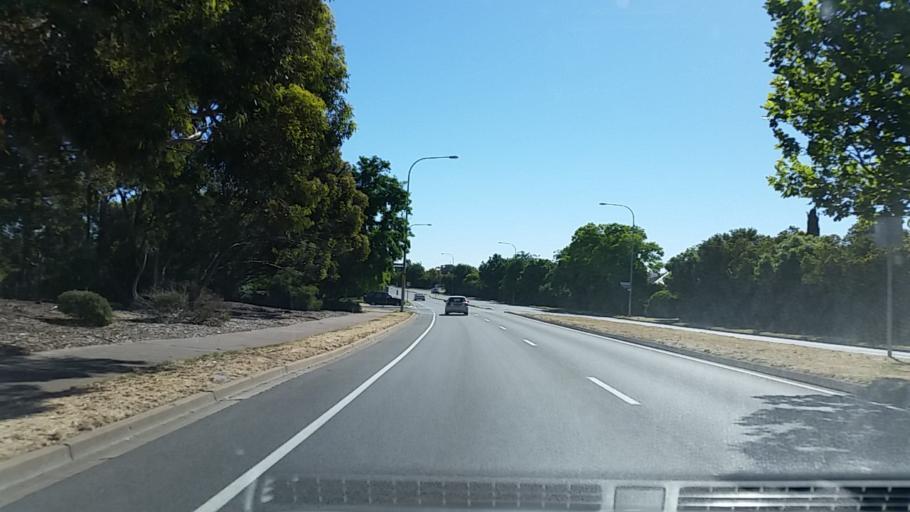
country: AU
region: South Australia
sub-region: Tea Tree Gully
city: Modbury
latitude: -34.7941
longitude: 138.6910
